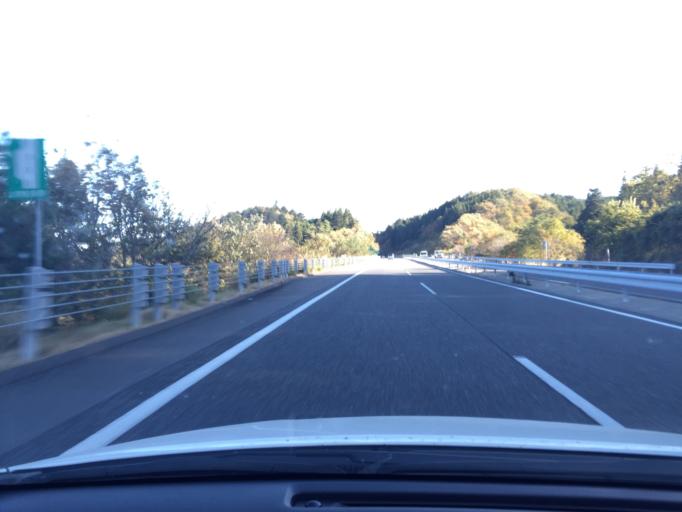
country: JP
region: Fukushima
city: Funehikimachi-funehiki
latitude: 37.2507
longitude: 140.6596
